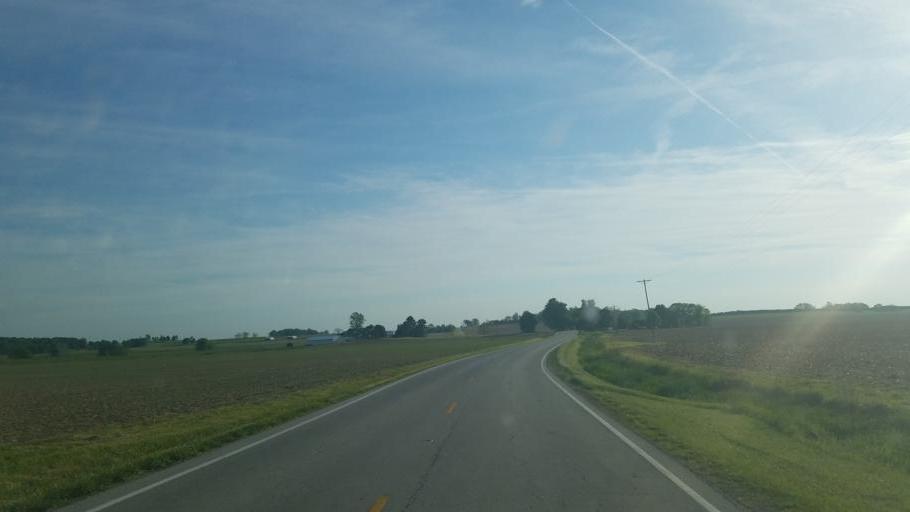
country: US
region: Ohio
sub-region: Highland County
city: Greenfield
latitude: 39.4030
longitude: -83.3078
